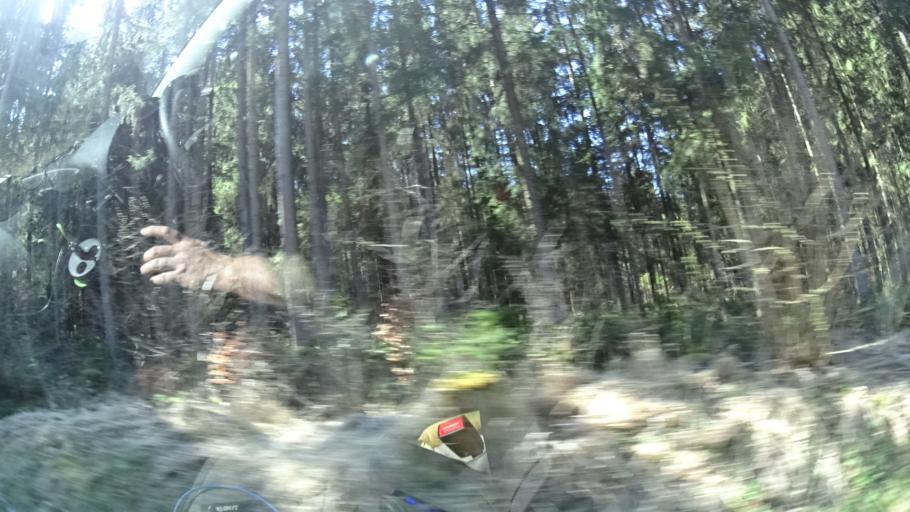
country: DE
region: Bavaria
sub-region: Upper Palatinate
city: Kastl
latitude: 49.3850
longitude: 11.6886
